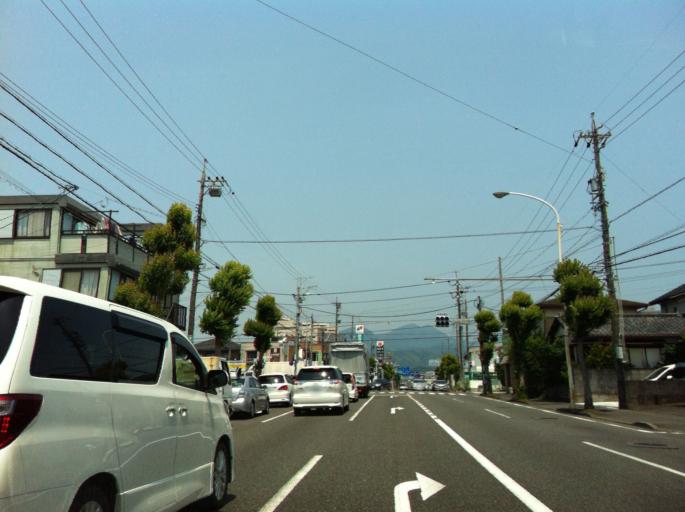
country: JP
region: Shizuoka
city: Shizuoka-shi
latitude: 34.9826
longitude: 138.4230
